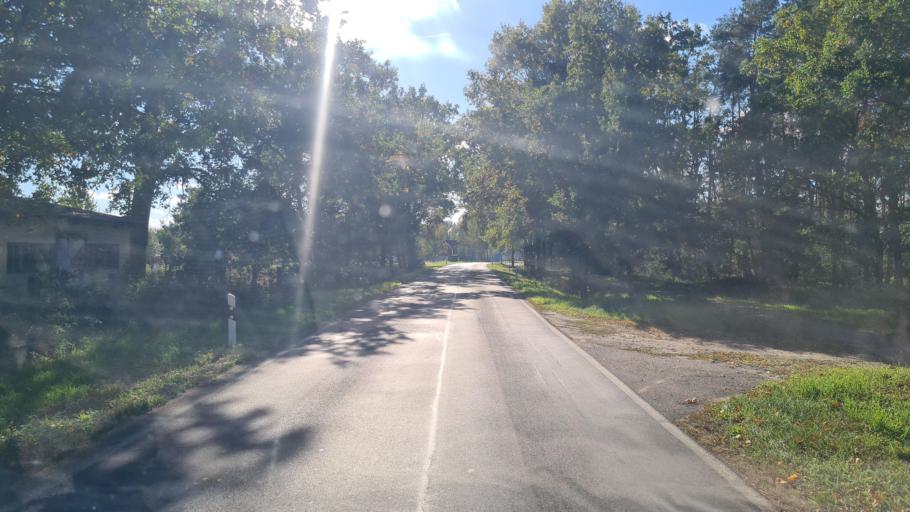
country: DE
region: Brandenburg
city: Kolkwitz
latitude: 51.7632
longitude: 14.2616
